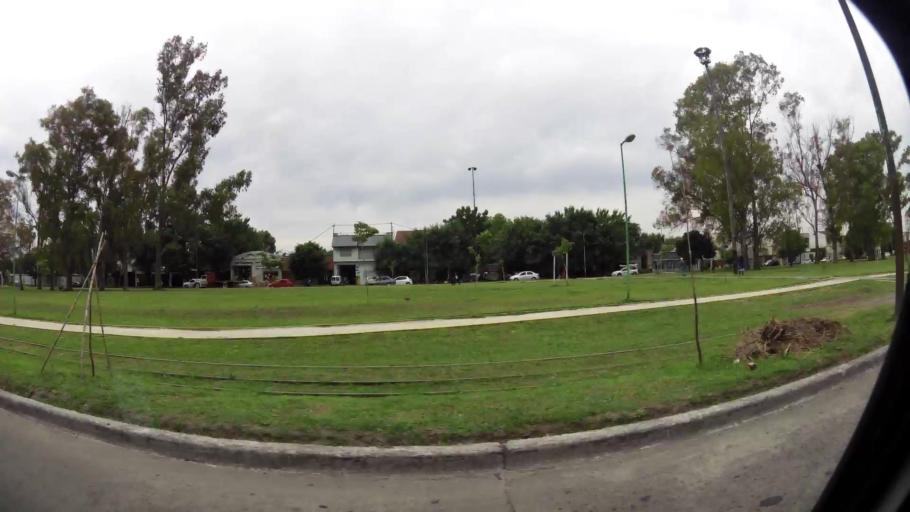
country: AR
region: Buenos Aires
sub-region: Partido de La Plata
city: La Plata
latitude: -34.9455
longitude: -57.9645
